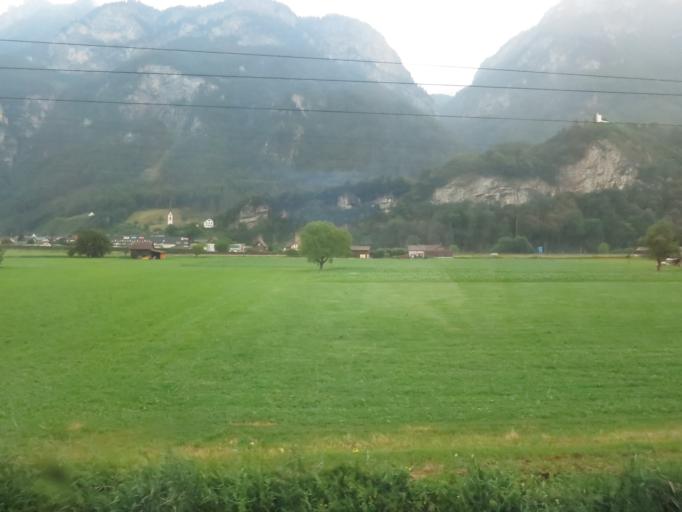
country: CH
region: Saint Gallen
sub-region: Wahlkreis Sarganserland
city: Flums
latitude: 47.1005
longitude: 9.3433
